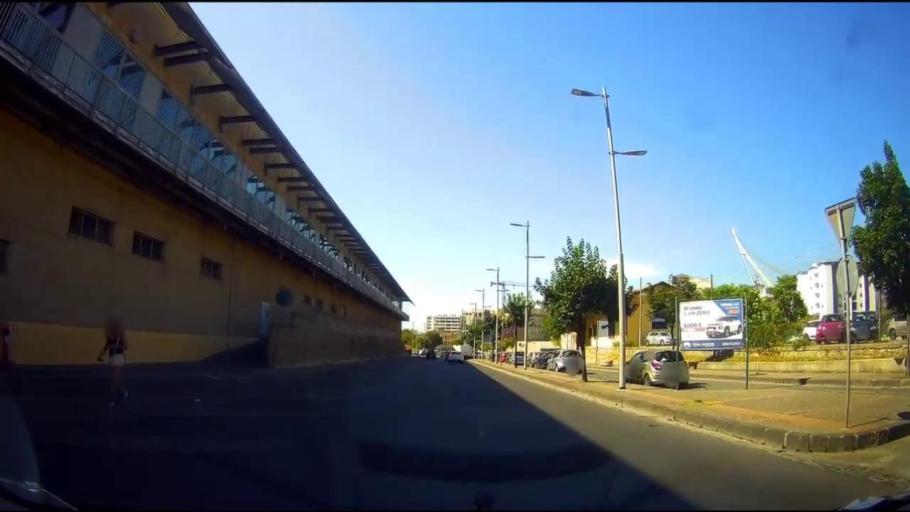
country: IT
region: Calabria
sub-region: Provincia di Cosenza
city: Cosenza
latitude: 39.2952
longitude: 16.2575
